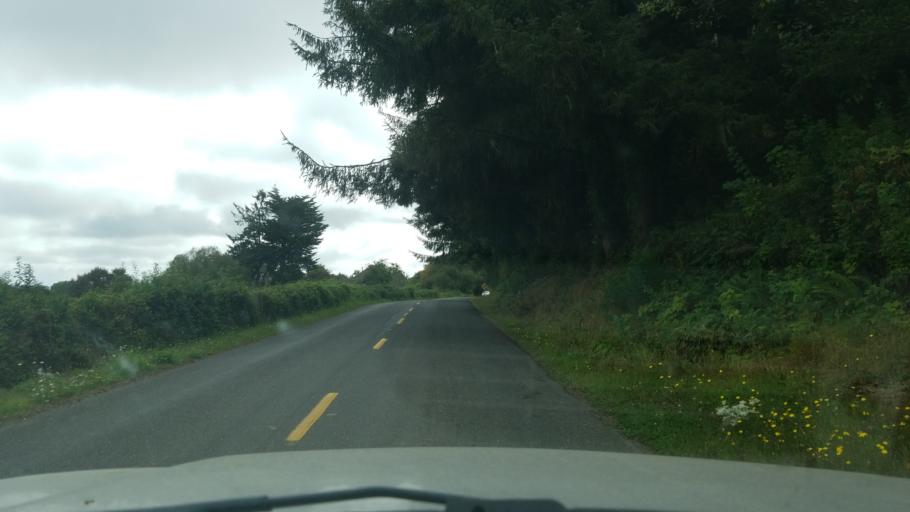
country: US
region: California
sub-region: Humboldt County
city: Ferndale
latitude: 40.5796
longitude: -124.2720
